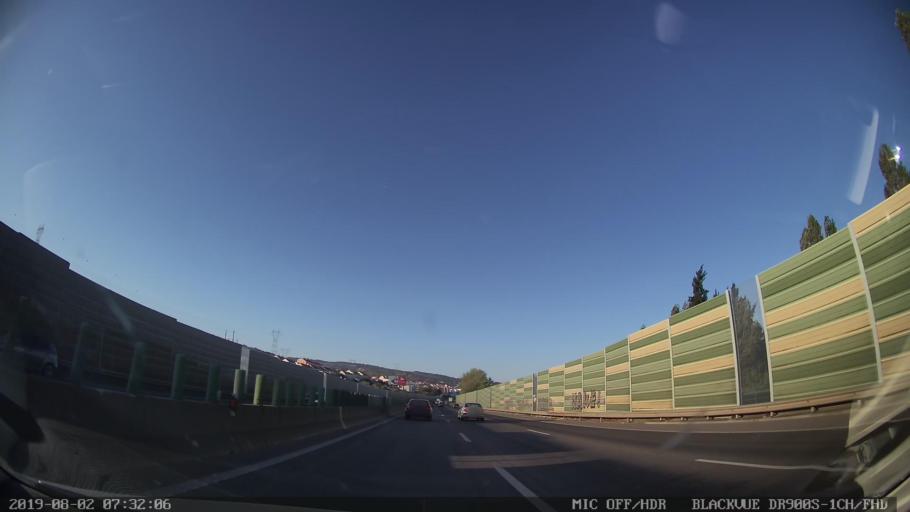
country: PT
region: Lisbon
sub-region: Vila Franca de Xira
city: Sobralinho
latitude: 38.9005
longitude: -9.0469
